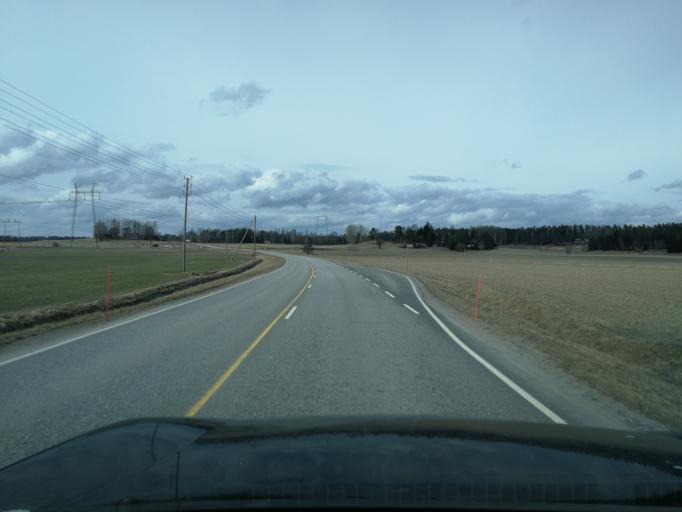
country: FI
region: Uusimaa
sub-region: Helsinki
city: Siuntio
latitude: 60.1168
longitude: 24.2412
